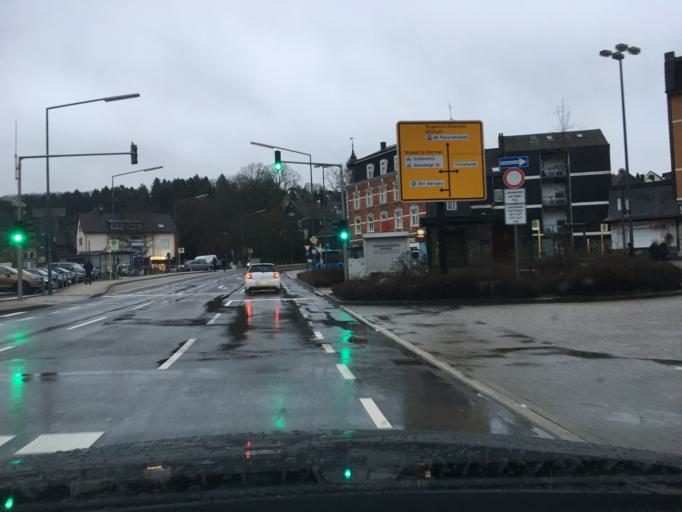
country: DE
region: North Rhine-Westphalia
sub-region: Regierungsbezirk Dusseldorf
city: Velbert
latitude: 51.3128
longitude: 7.0893
